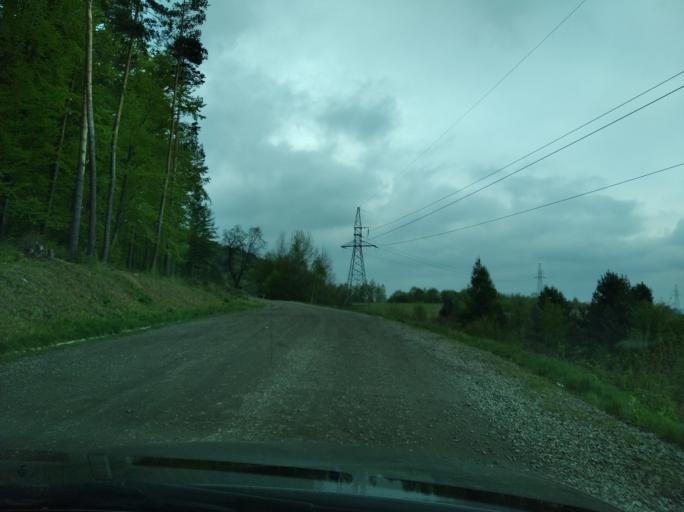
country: PL
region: Subcarpathian Voivodeship
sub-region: Powiat sanocki
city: Sanok
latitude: 49.5655
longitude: 22.2320
